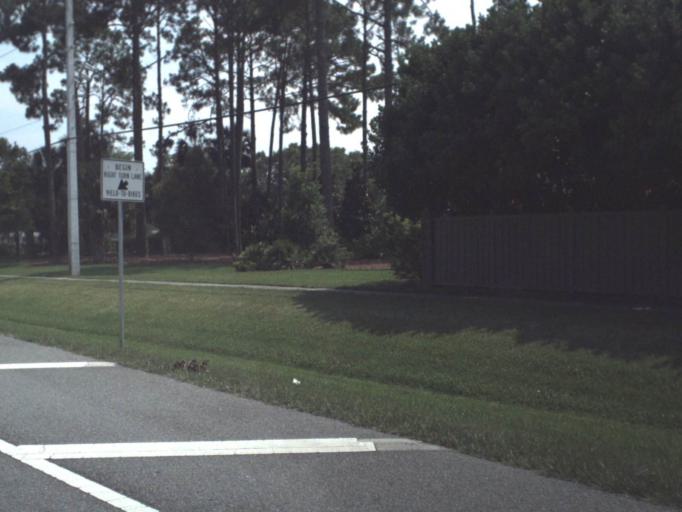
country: US
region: Florida
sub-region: Saint Johns County
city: Ponte Vedra Beach
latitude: 30.2175
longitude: -81.3819
